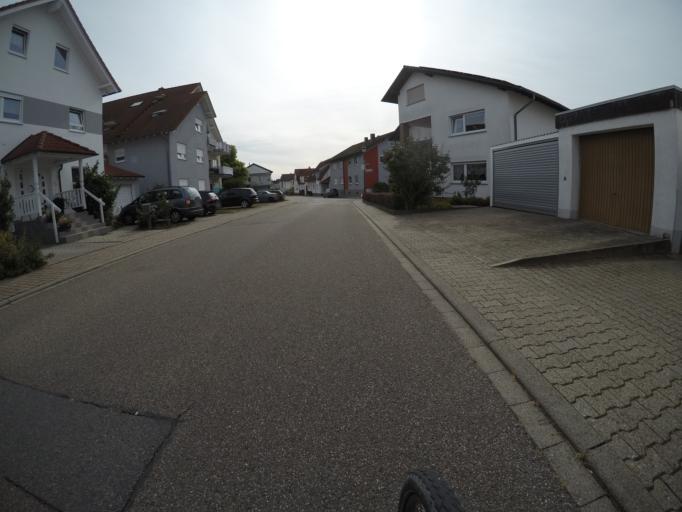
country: DE
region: Baden-Wuerttemberg
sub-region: Karlsruhe Region
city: Kronau
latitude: 49.2245
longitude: 8.6295
